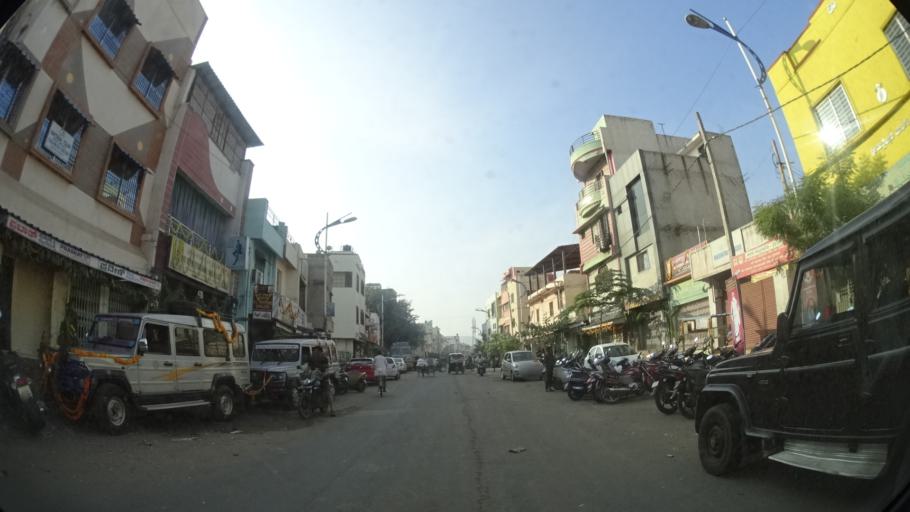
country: IN
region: Karnataka
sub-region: Bellary
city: Hospet
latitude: 15.2699
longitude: 76.3923
